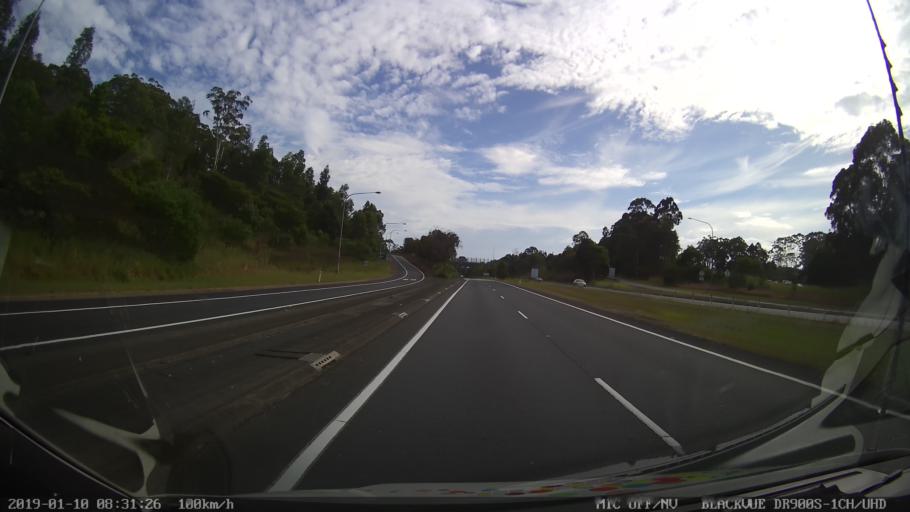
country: AU
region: New South Wales
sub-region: Coffs Harbour
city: Boambee
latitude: -30.3564
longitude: 153.0612
